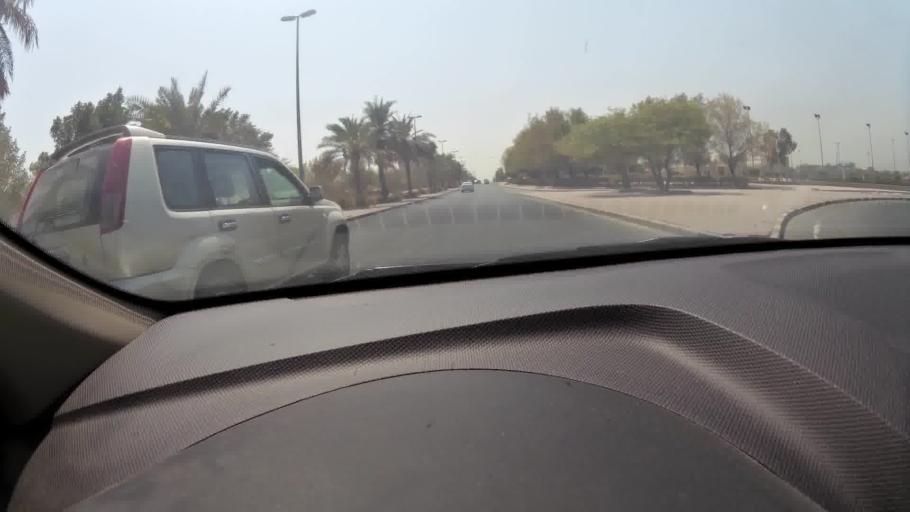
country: KW
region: Al Farwaniyah
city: Al Farwaniyah
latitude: 29.2593
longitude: 47.9465
